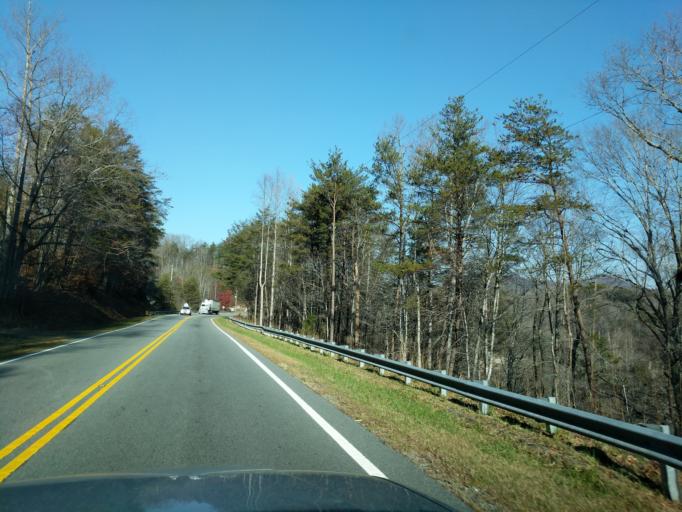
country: US
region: North Carolina
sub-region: McDowell County
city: West Marion
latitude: 35.5457
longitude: -81.9620
